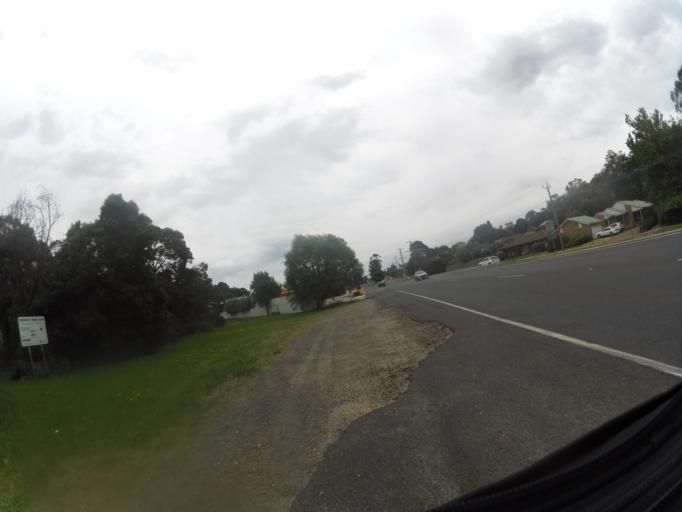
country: AU
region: Victoria
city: Brown Hill
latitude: -37.4181
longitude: 143.8942
